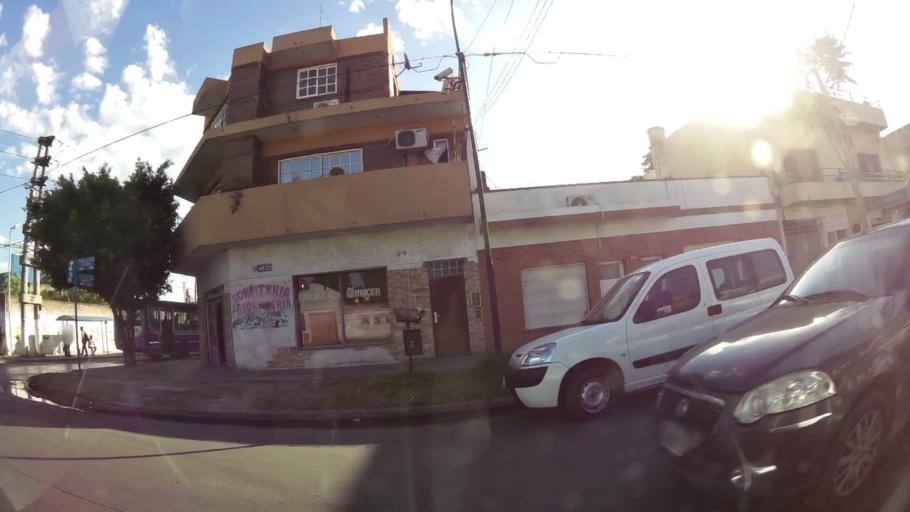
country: AR
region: Buenos Aires
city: Hurlingham
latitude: -34.5638
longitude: -58.6122
